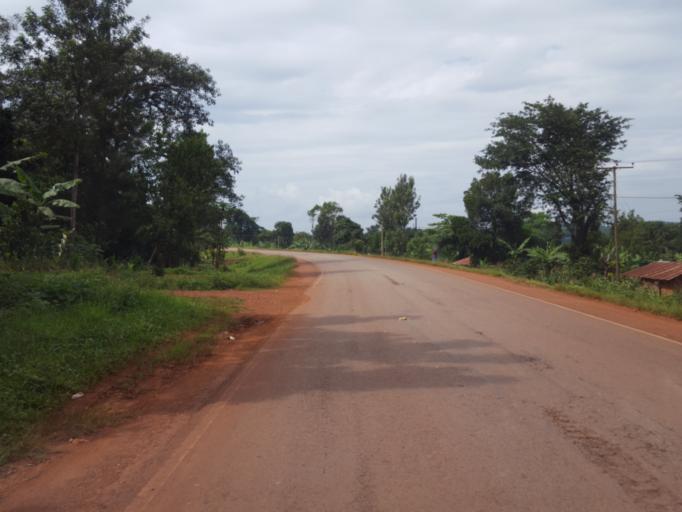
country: UG
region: Central Region
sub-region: Mityana District
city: Mityana
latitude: 0.6416
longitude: 32.0976
